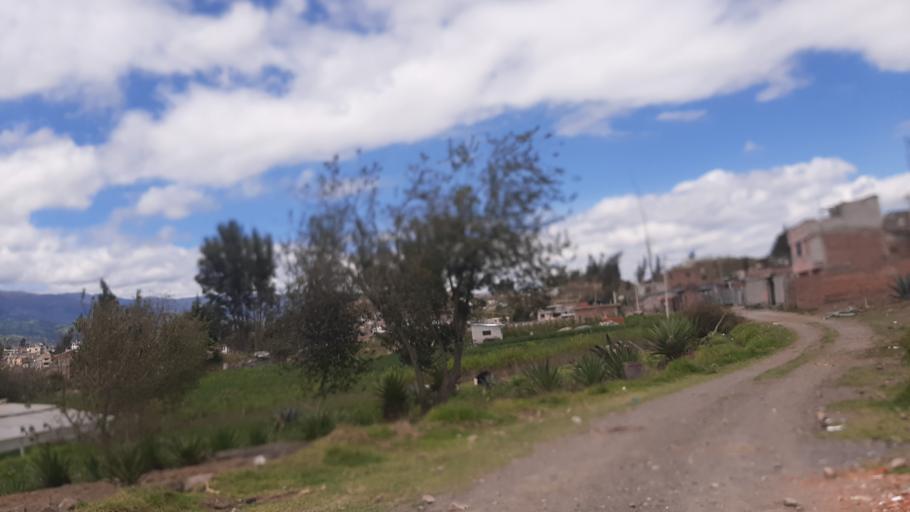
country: EC
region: Chimborazo
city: Riobamba
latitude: -1.6528
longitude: -78.6312
